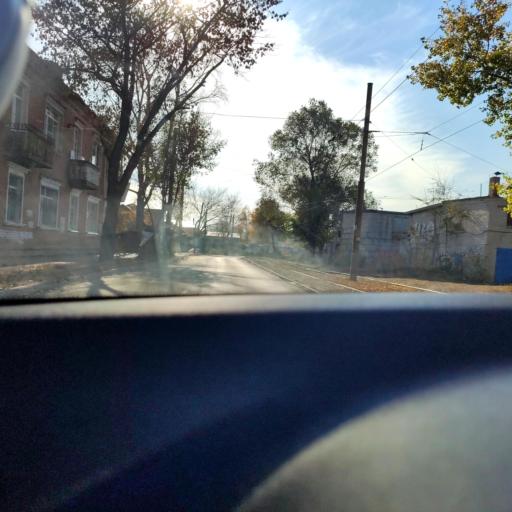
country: RU
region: Samara
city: Petra-Dubrava
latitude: 53.2295
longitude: 50.2838
